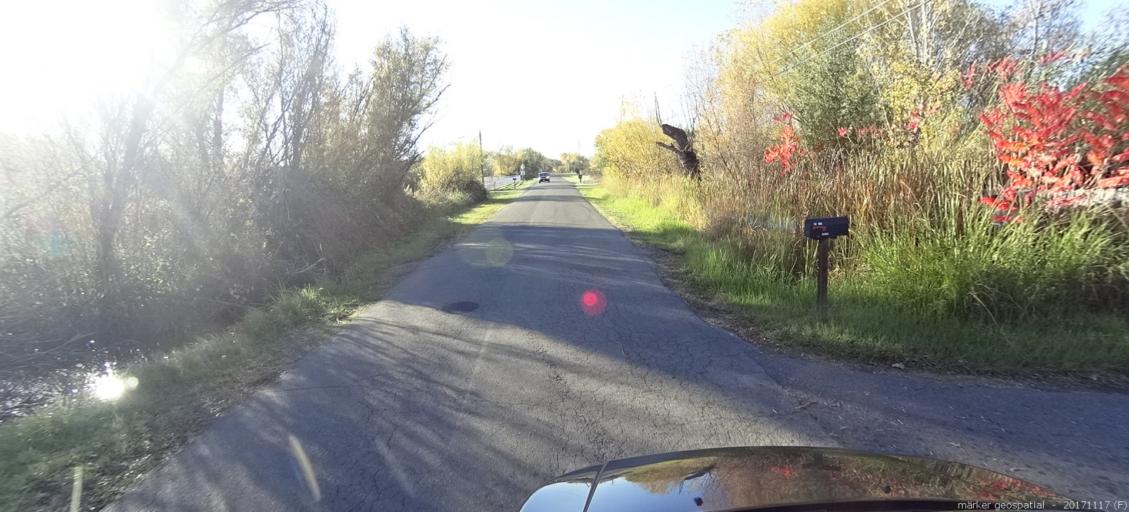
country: US
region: California
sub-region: Shasta County
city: Cottonwood
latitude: 40.4162
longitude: -122.2390
